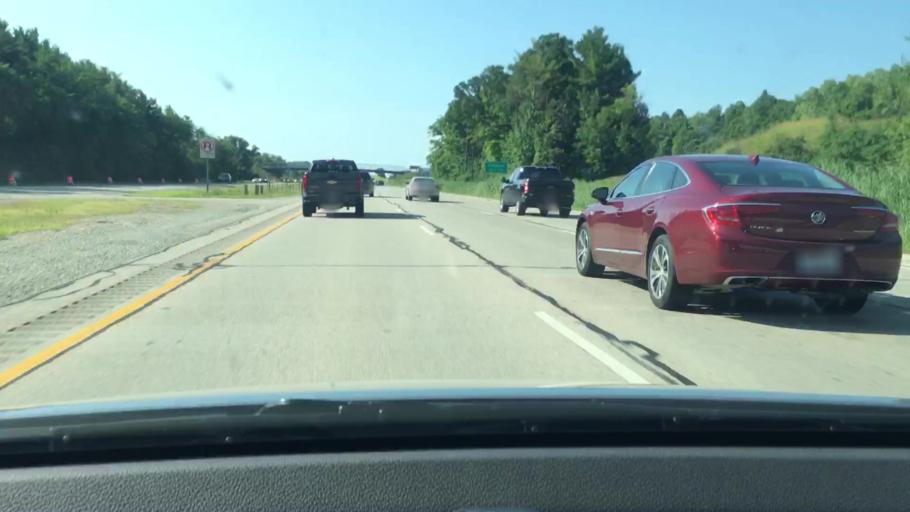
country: US
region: Wisconsin
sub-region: Outagamie County
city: Appleton
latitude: 44.2878
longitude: -88.4664
